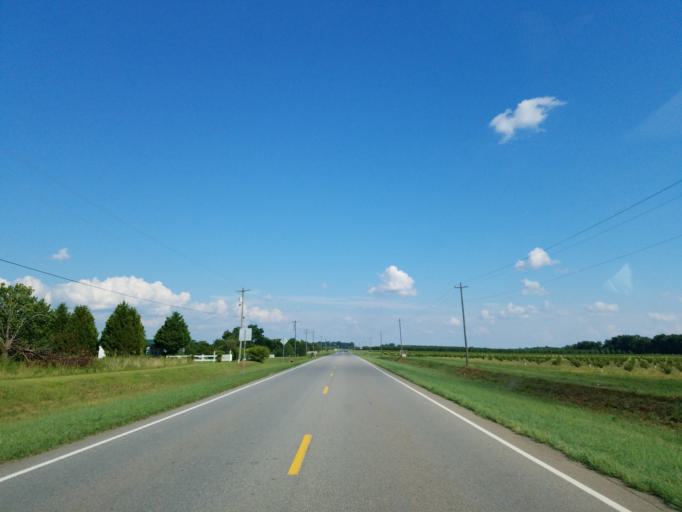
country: US
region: Georgia
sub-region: Peach County
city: Fort Valley
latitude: 32.6114
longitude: -83.9533
